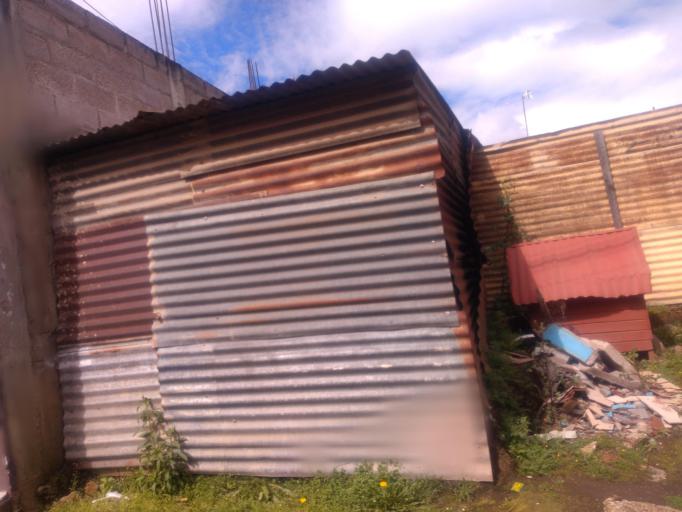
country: GT
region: Quetzaltenango
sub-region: Municipio de La Esperanza
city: La Esperanza
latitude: 14.8620
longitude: -91.5694
